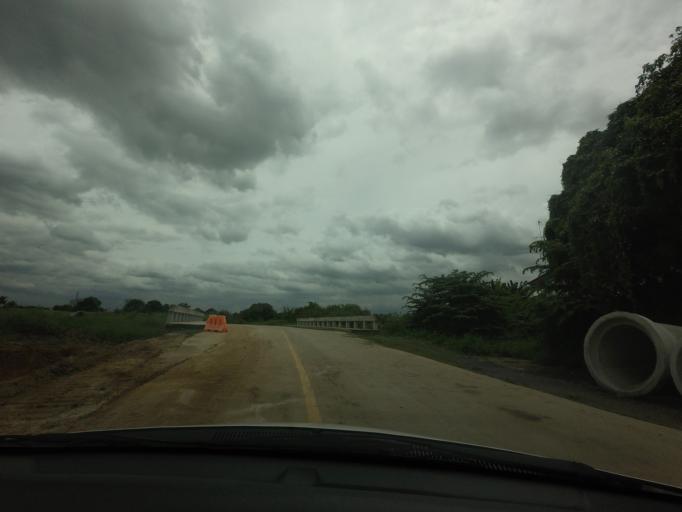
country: TH
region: Bangkok
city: Min Buri
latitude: 13.7783
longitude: 100.7614
